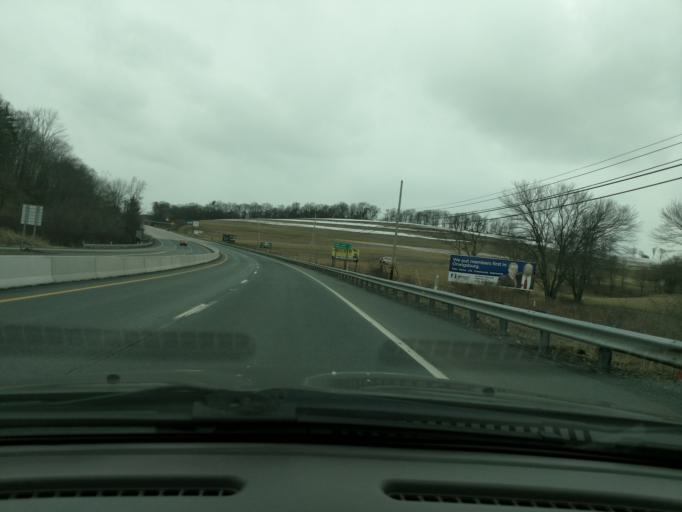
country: US
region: Pennsylvania
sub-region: Berks County
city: West Hamburg
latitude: 40.6107
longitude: -76.0318
